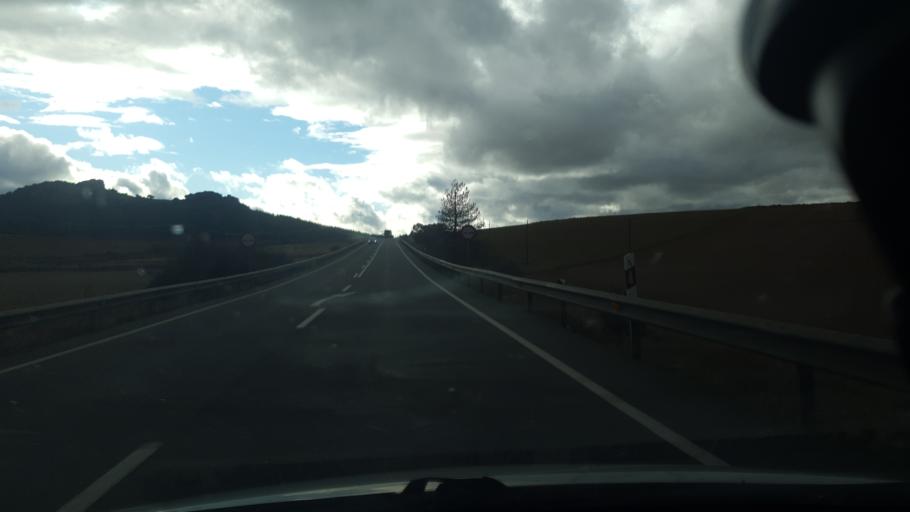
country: ES
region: Castille and Leon
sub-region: Provincia de Avila
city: Ojos-Albos
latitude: 40.7375
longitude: -4.4862
